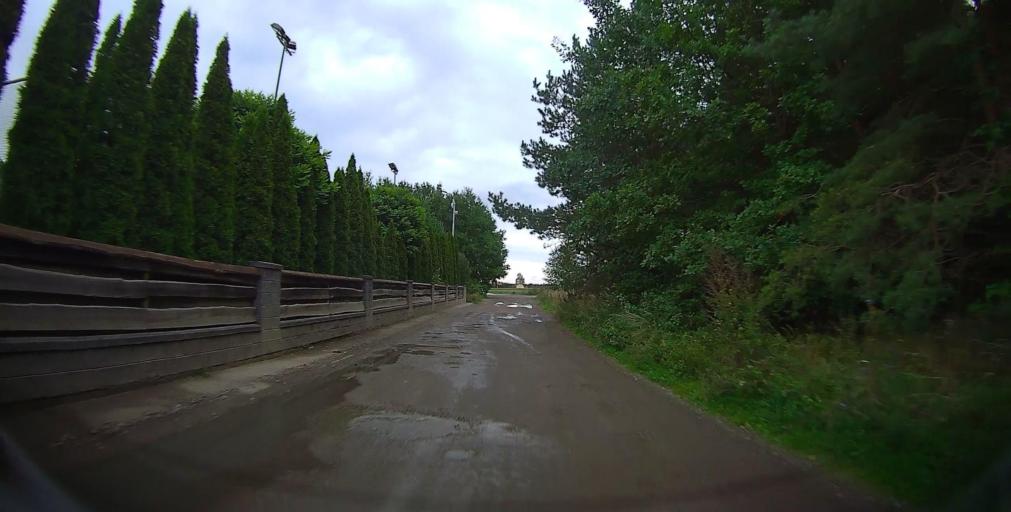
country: PL
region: Masovian Voivodeship
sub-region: Powiat radomski
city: Jedlinsk
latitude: 51.4593
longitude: 21.1022
